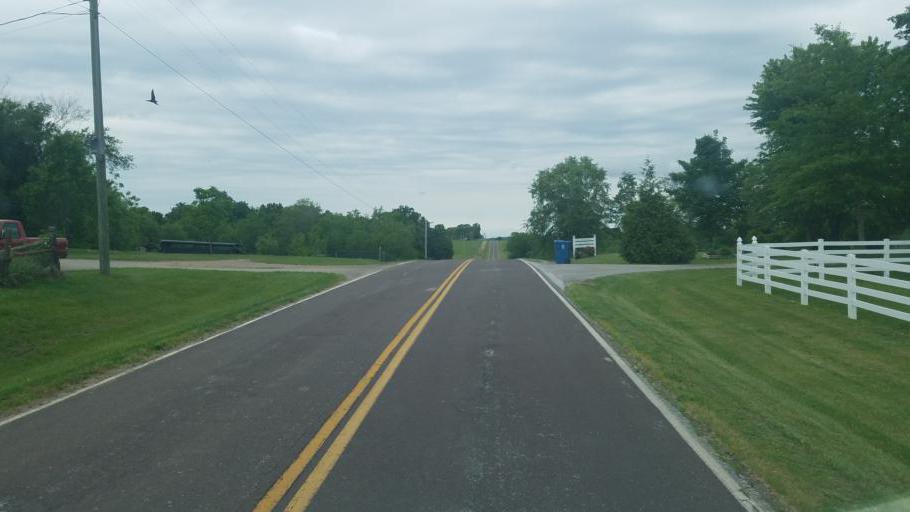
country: US
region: Missouri
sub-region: Moniteau County
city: Tipton
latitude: 38.5716
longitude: -92.6951
